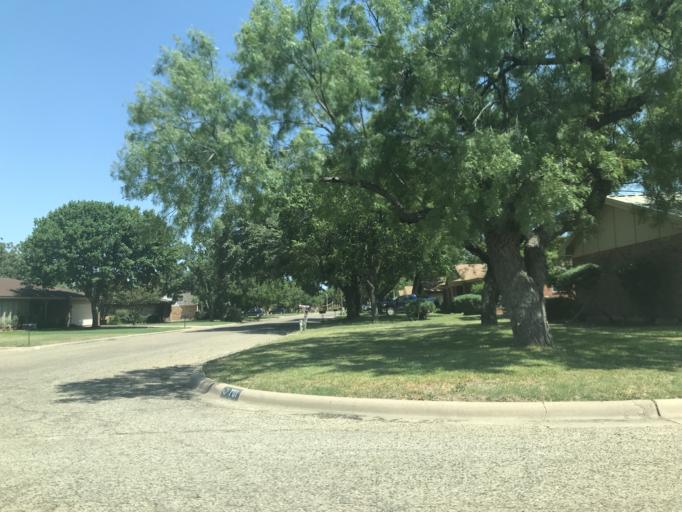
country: US
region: Texas
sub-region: Taylor County
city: Abilene
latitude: 32.4541
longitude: -99.7014
